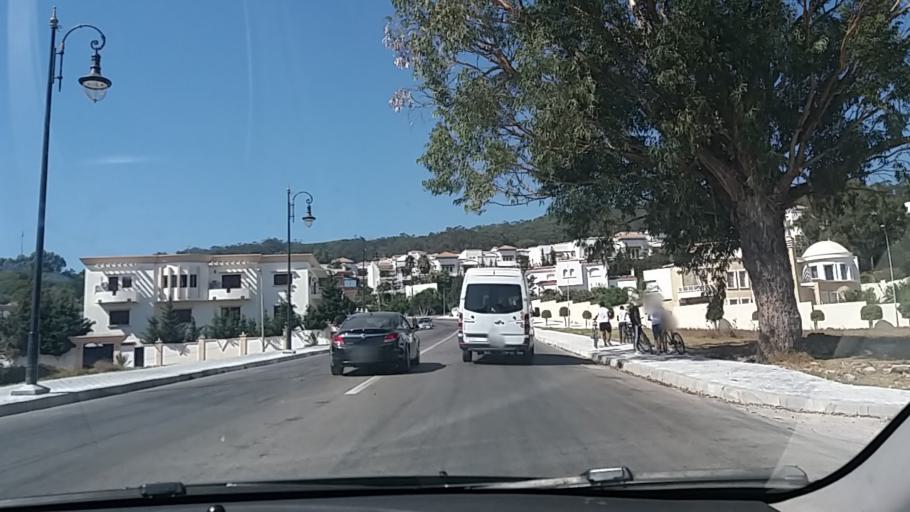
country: MA
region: Tanger-Tetouan
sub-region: Tanger-Assilah
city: Boukhalef
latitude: 35.7800
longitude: -5.8607
